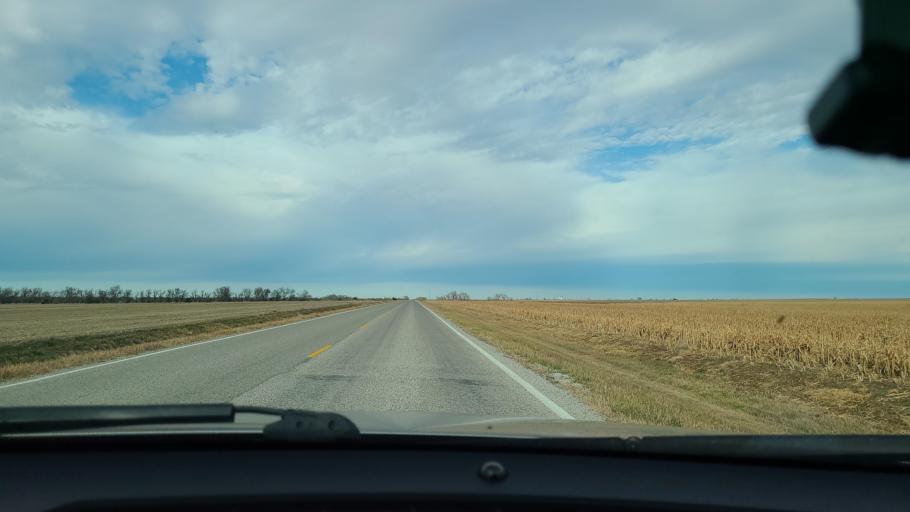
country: US
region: Kansas
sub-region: McPherson County
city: Inman
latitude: 38.3293
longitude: -97.9246
